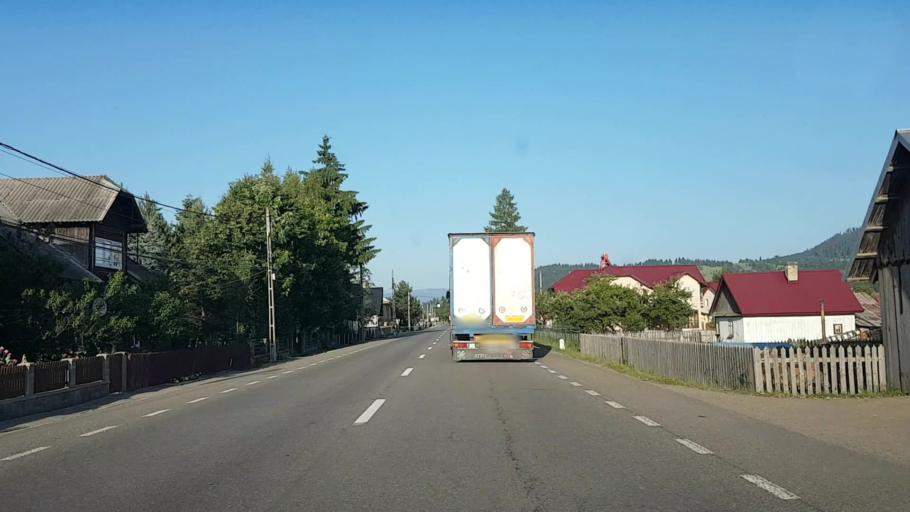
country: RO
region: Suceava
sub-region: Comuna Dorna Candrenilor
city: Dorna Candrenilor
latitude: 47.3564
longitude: 25.2396
